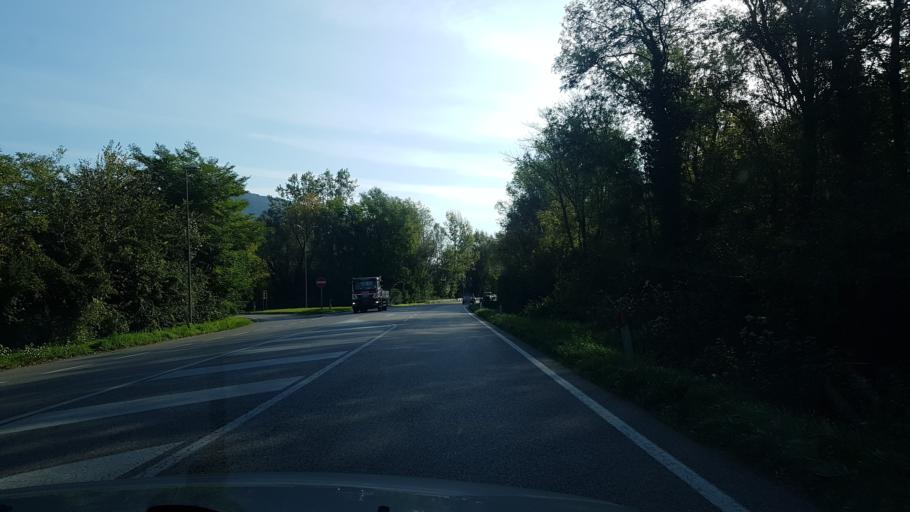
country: IT
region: Friuli Venezia Giulia
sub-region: Provincia di Udine
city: Artegna
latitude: 46.2439
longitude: 13.1346
